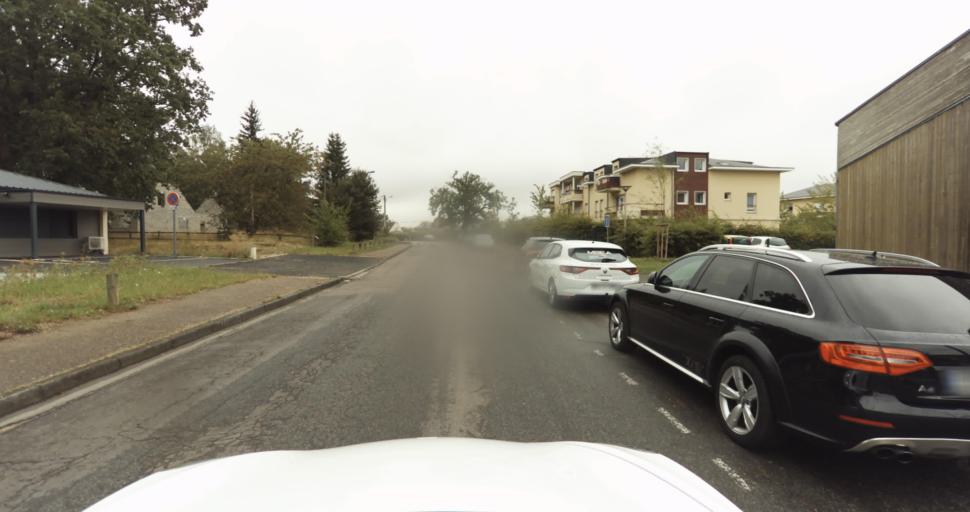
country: FR
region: Haute-Normandie
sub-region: Departement de l'Eure
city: Evreux
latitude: 49.0333
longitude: 1.1349
